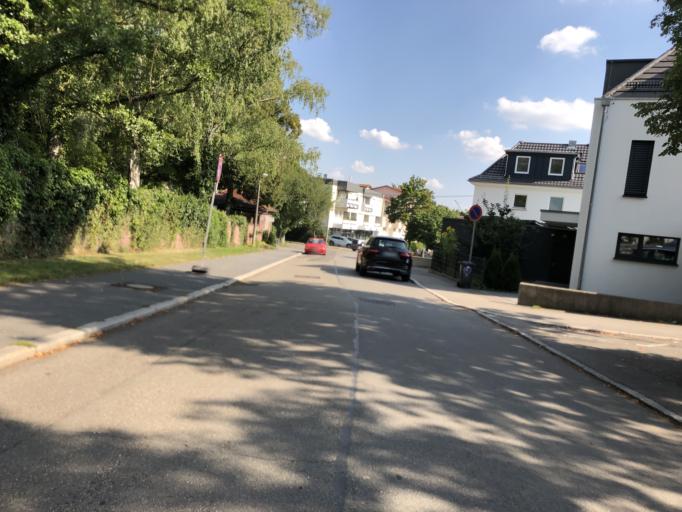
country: DE
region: Baden-Wuerttemberg
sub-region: Regierungsbezirk Stuttgart
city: Sindelfingen
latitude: 48.7126
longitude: 9.0127
